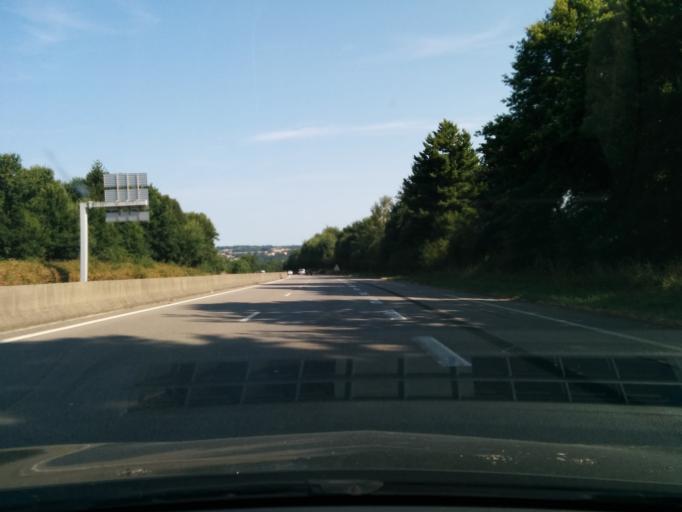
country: FR
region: Limousin
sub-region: Departement de la Haute-Vienne
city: Boisseuil
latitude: 45.7523
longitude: 1.3344
